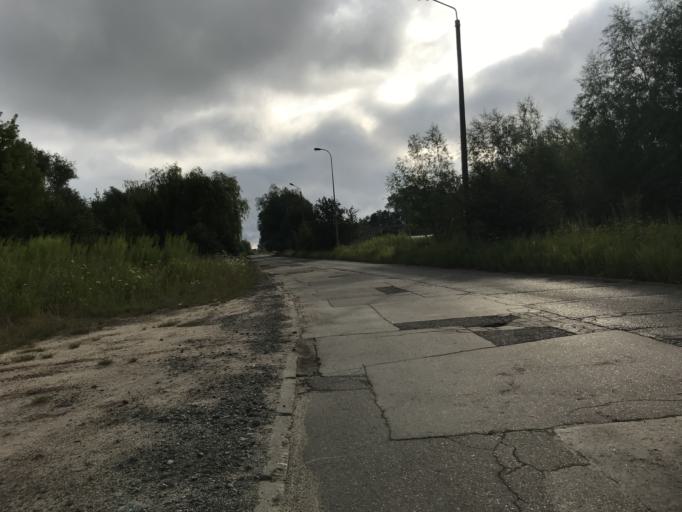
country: PL
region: Pomeranian Voivodeship
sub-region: Gdansk
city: Gdansk
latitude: 54.3386
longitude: 18.6846
